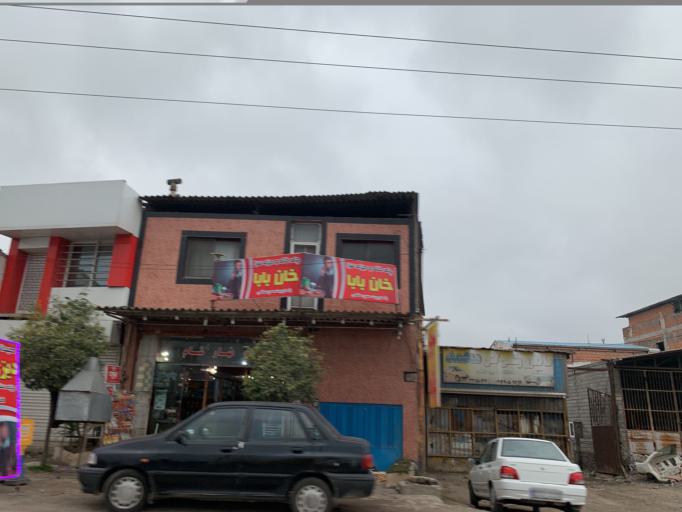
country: IR
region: Mazandaran
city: Babol
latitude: 36.5308
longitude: 52.6365
